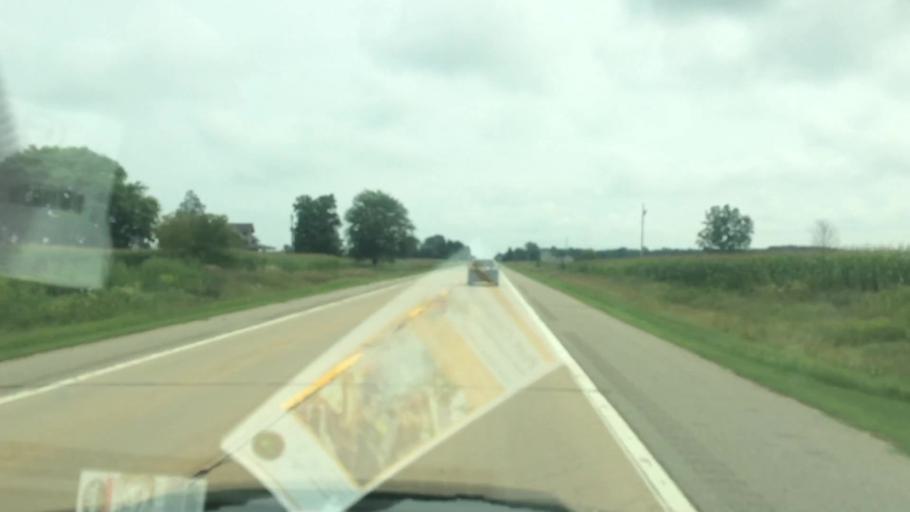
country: US
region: Michigan
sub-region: Huron County
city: Bad Axe
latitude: 44.0427
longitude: -82.9354
